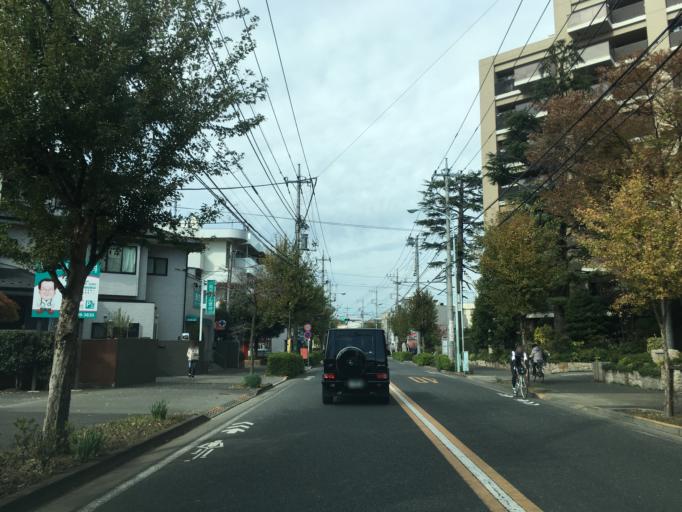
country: JP
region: Tokyo
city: Chofugaoka
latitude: 35.6361
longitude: 139.5764
